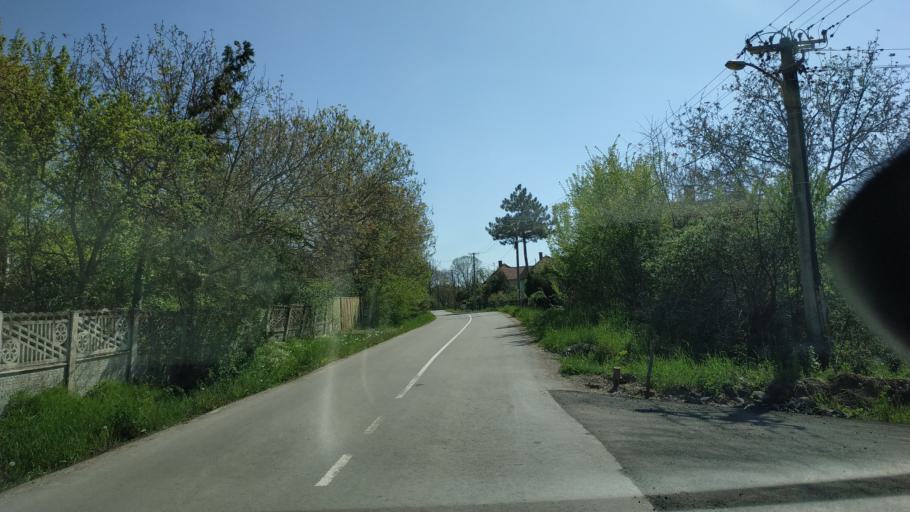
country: RS
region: Central Serbia
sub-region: Nisavski Okrug
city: Nis
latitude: 43.4634
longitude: 21.8616
